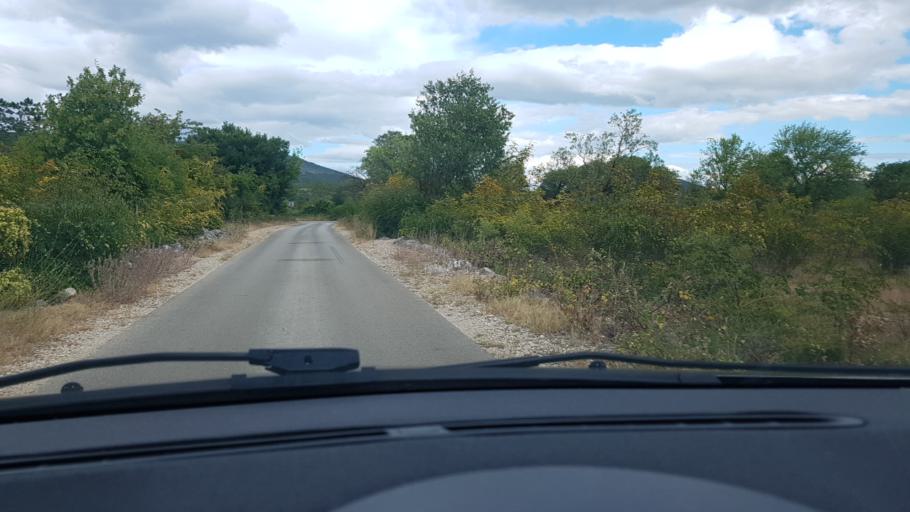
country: HR
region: Sibensko-Kniniska
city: Kistanje
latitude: 44.1072
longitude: 15.9372
